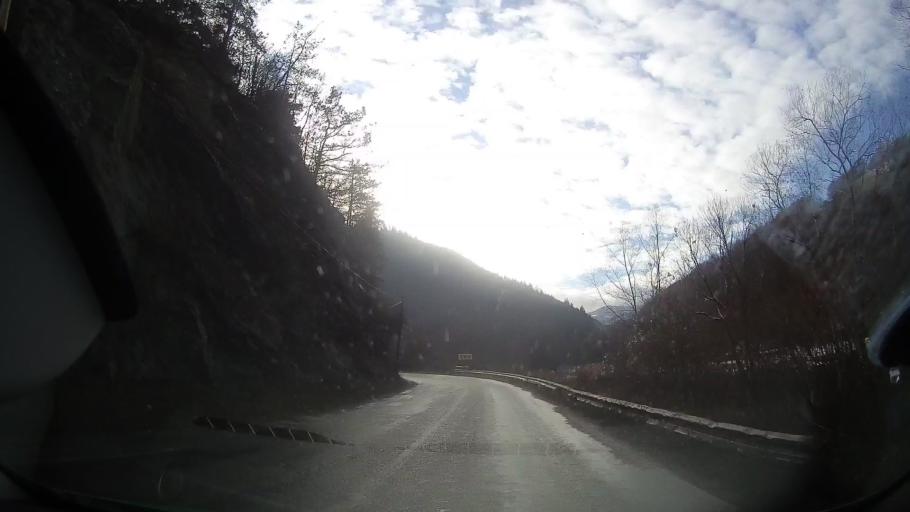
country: RO
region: Alba
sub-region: Comuna Bistra
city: Bistra
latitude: 46.3804
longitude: 23.1456
